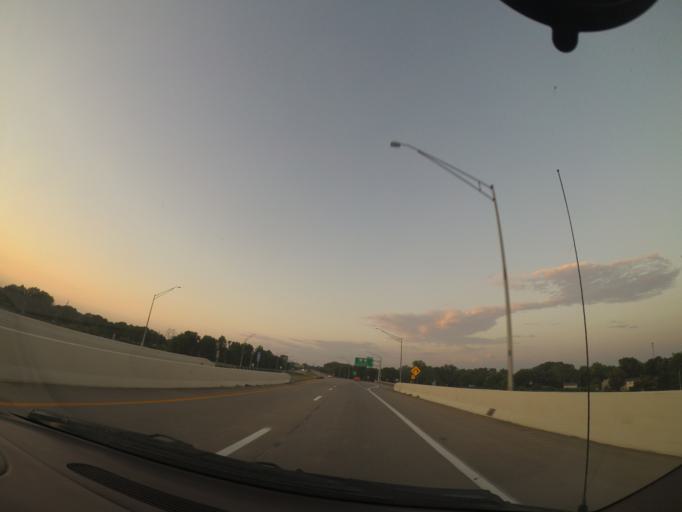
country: US
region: Ohio
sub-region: Lake County
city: Painesville
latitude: 41.7293
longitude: -81.2597
